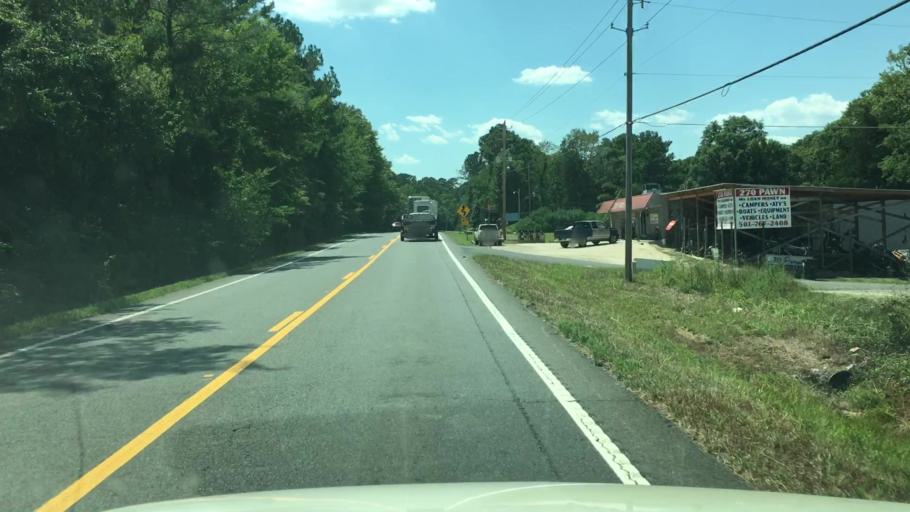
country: US
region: Arkansas
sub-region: Garland County
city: Piney
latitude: 34.5095
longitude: -93.1634
